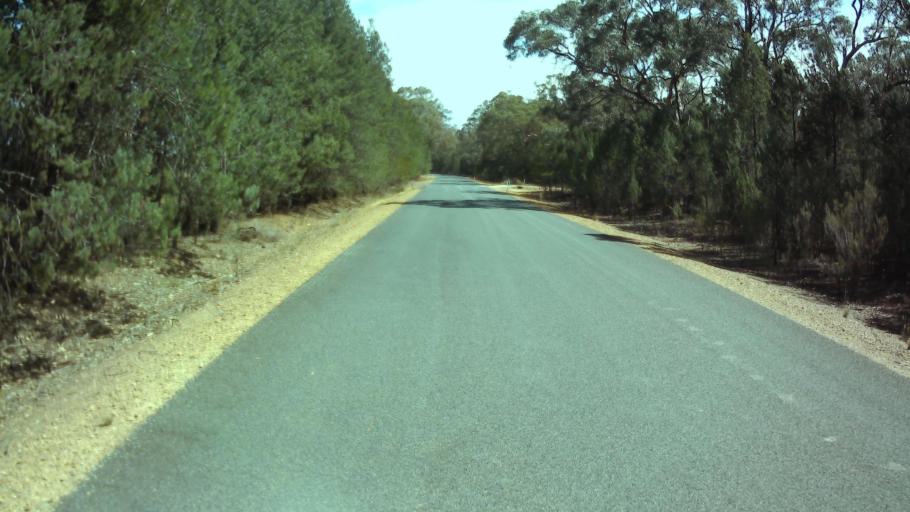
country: AU
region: New South Wales
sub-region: Weddin
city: Grenfell
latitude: -34.0111
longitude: 148.1297
